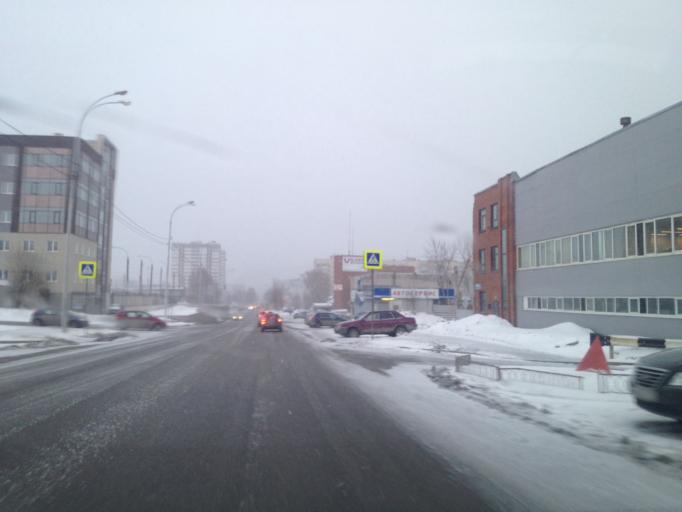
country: RU
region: Sverdlovsk
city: Sovkhoznyy
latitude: 56.8125
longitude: 60.5401
